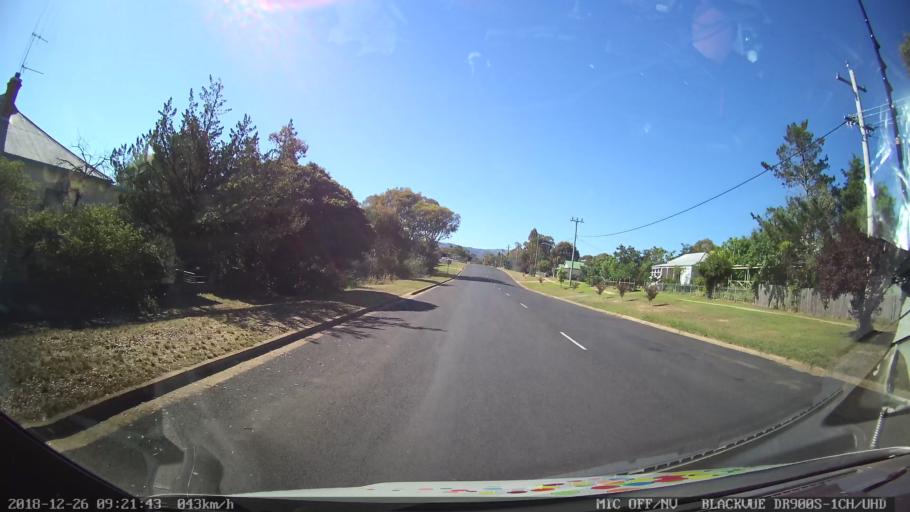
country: AU
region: New South Wales
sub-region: Mid-Western Regional
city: Kandos
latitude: -32.8020
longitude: 149.9740
